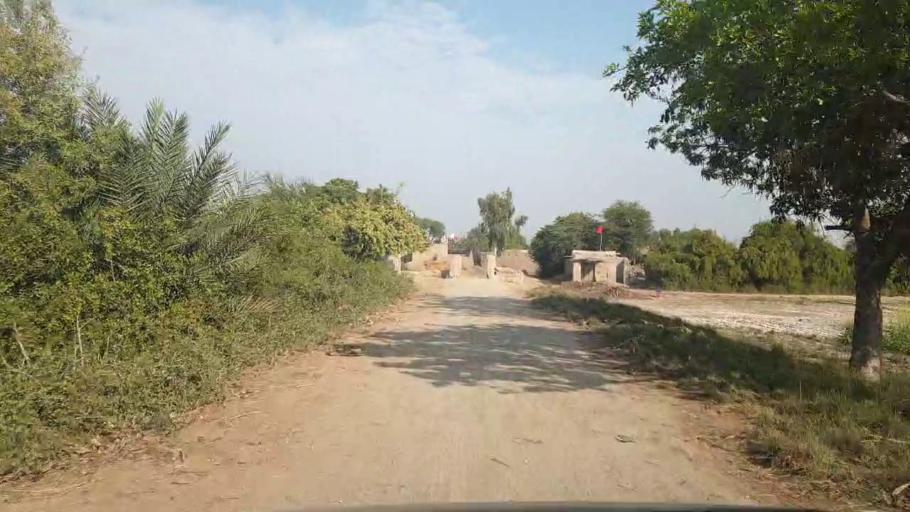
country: PK
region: Sindh
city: Tando Adam
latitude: 25.7606
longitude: 68.5882
